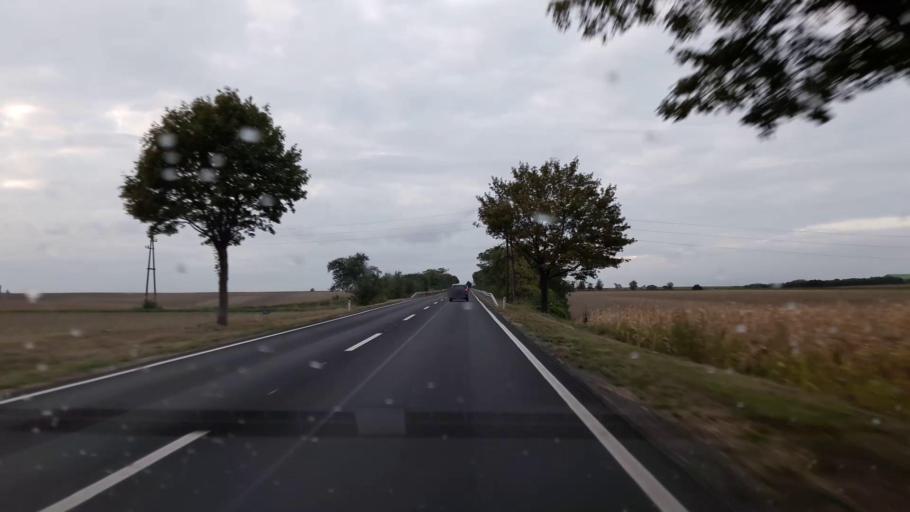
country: AT
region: Lower Austria
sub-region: Politischer Bezirk Wien-Umgebung
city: Schwadorf
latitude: 48.0809
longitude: 16.5685
